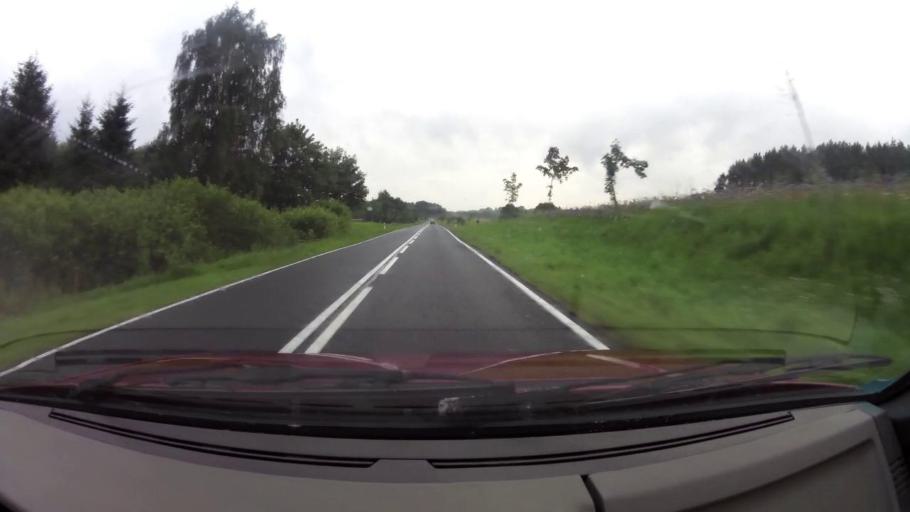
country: PL
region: West Pomeranian Voivodeship
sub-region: Powiat stargardzki
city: Chociwel
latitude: 53.4776
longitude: 15.3701
